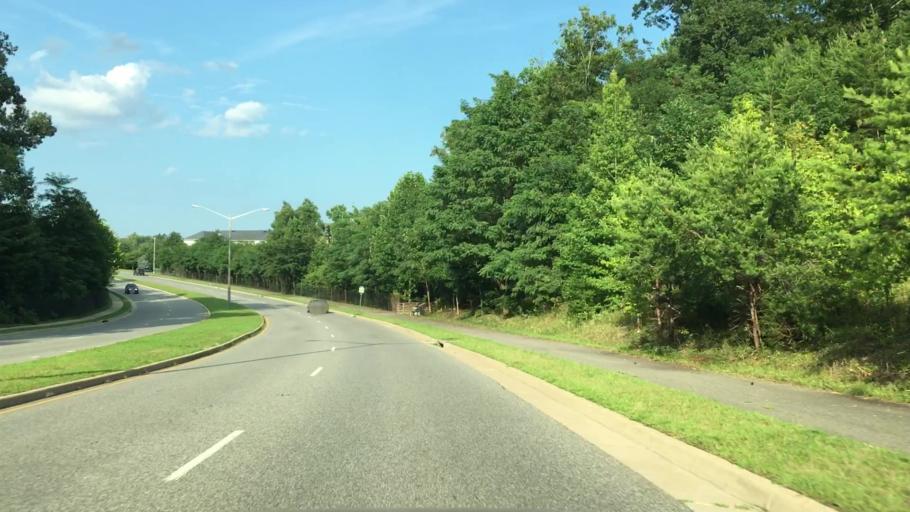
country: US
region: Virginia
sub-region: Stafford County
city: Falmouth
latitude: 38.3057
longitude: -77.4976
